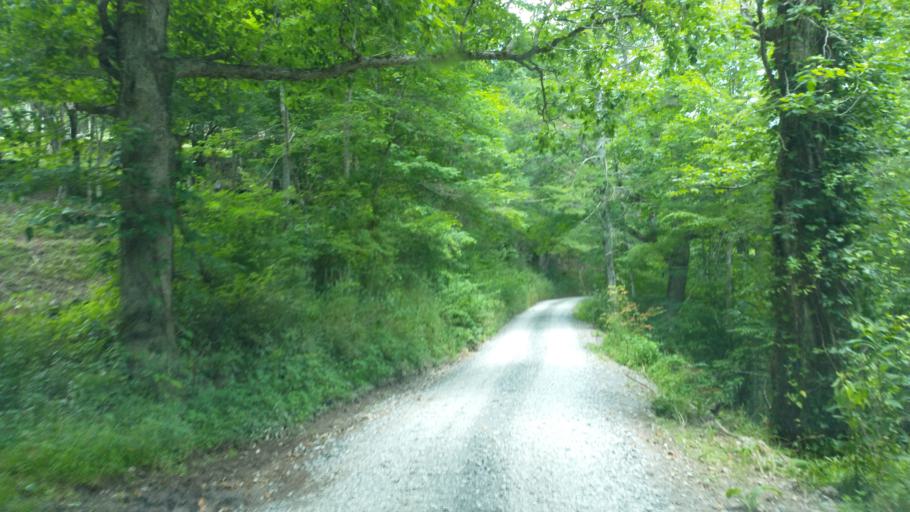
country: US
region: West Virginia
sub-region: Mercer County
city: Athens
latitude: 37.4361
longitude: -81.0024
